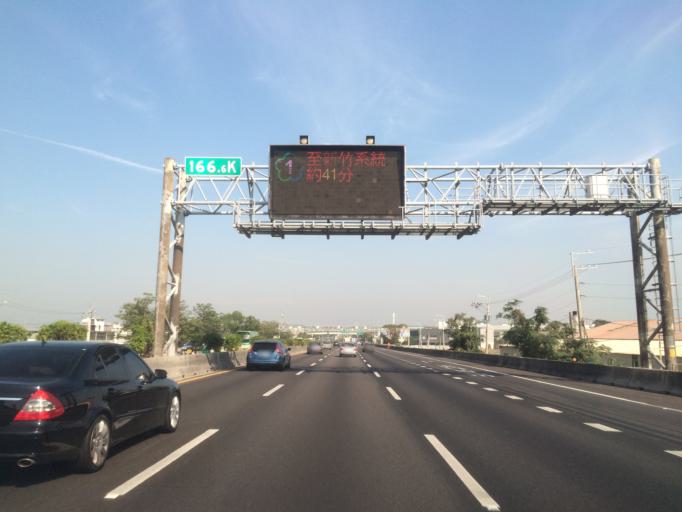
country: TW
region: Taiwan
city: Fengyuan
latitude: 24.2603
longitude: 120.6917
